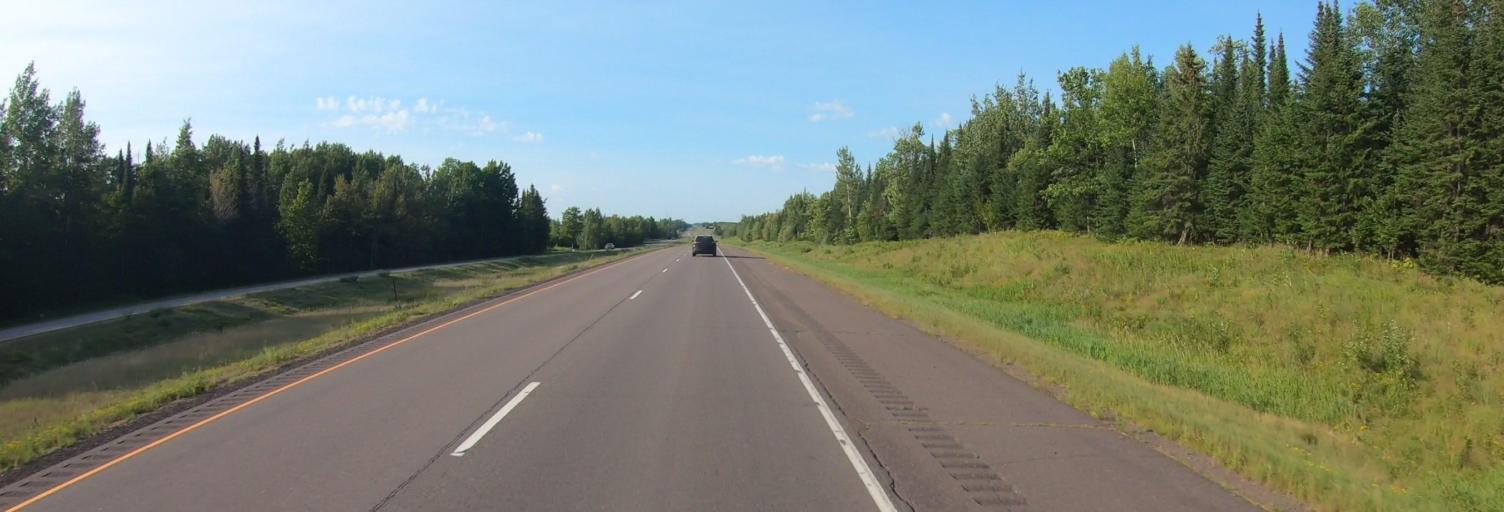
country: US
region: Minnesota
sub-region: Carlton County
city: Cloquet
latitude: 47.0137
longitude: -92.4709
